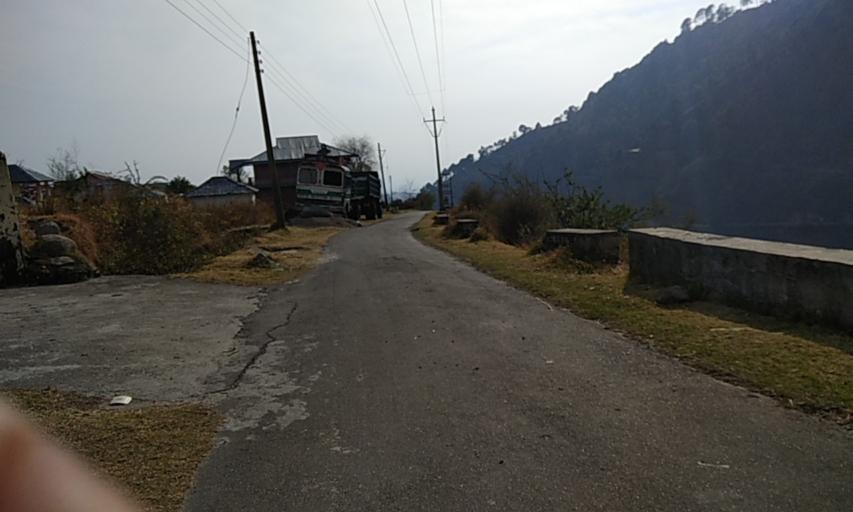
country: IN
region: Himachal Pradesh
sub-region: Kangra
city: Palampur
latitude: 32.1377
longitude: 76.5364
